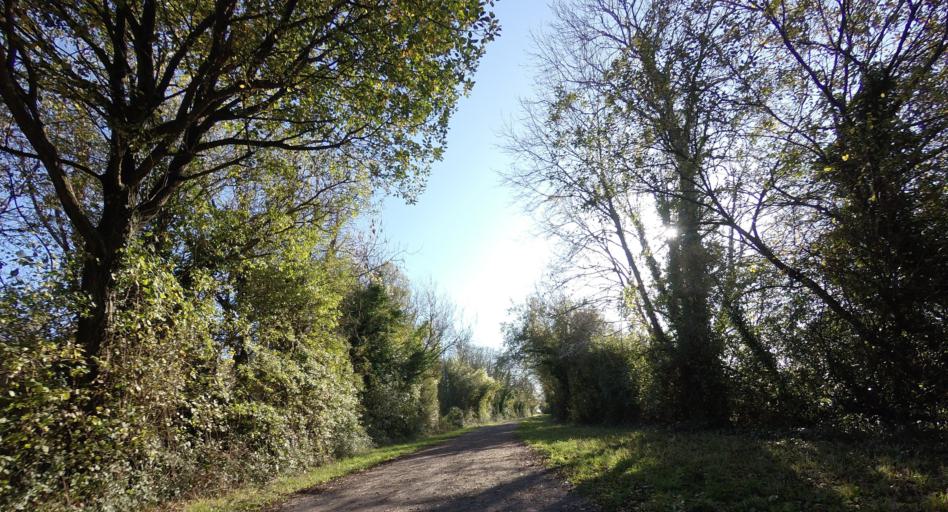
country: GB
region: England
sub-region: West Sussex
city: Shoreham-by-Sea
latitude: 50.8567
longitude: -0.2914
